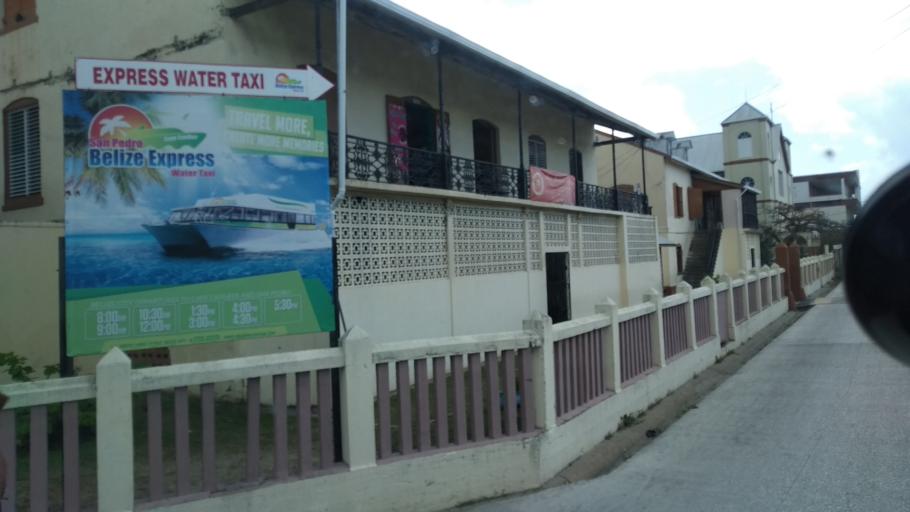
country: BZ
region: Belize
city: Belize City
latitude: 17.4968
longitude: -88.1877
